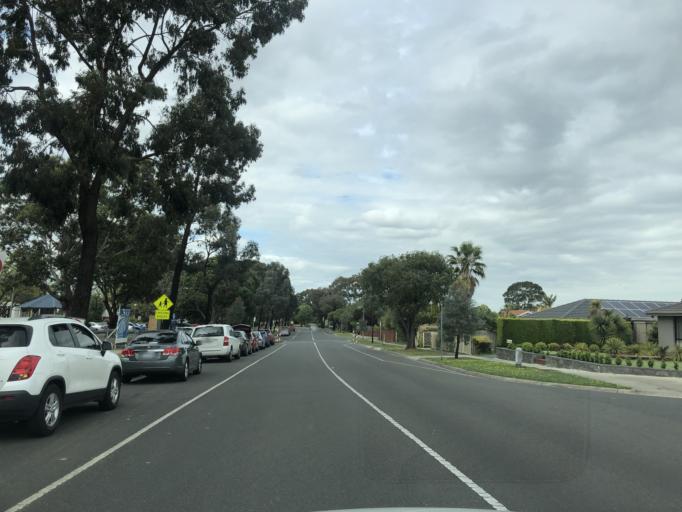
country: AU
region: Victoria
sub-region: Greater Dandenong
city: Noble Park North
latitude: -37.9334
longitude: 145.1956
